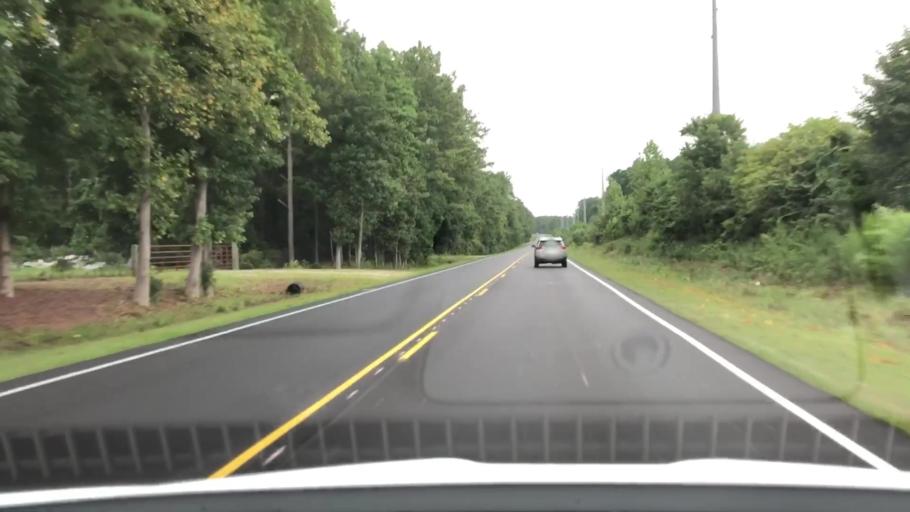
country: US
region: North Carolina
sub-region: Carteret County
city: Cape Carteret
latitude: 34.7621
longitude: -77.0953
